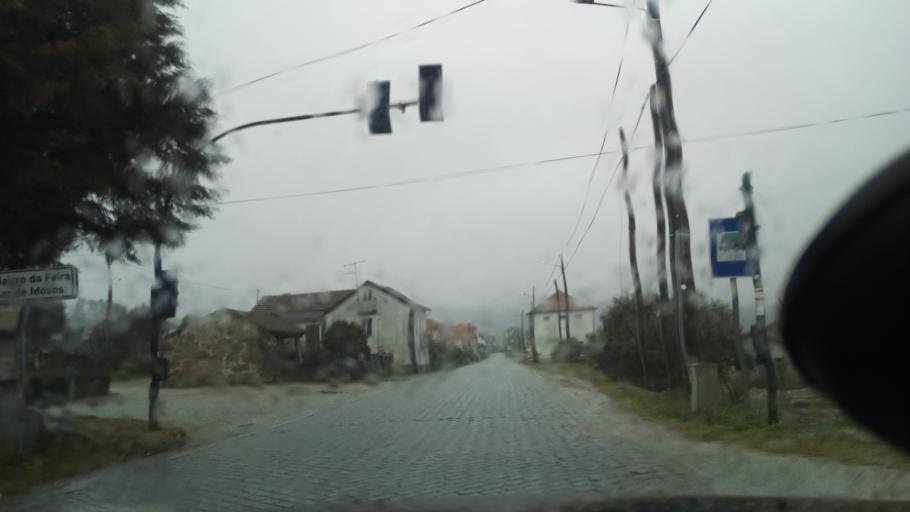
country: PT
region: Viseu
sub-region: Mangualde
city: Mangualde
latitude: 40.6114
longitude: -7.6768
